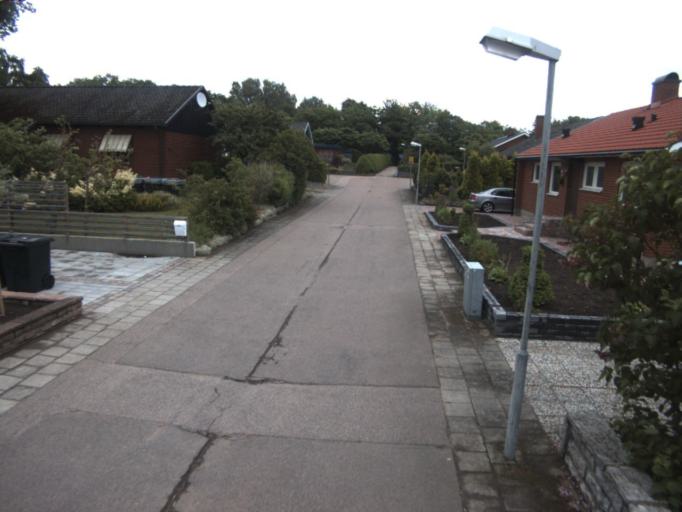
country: SE
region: Skane
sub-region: Helsingborg
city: Helsingborg
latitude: 56.0290
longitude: 12.7444
